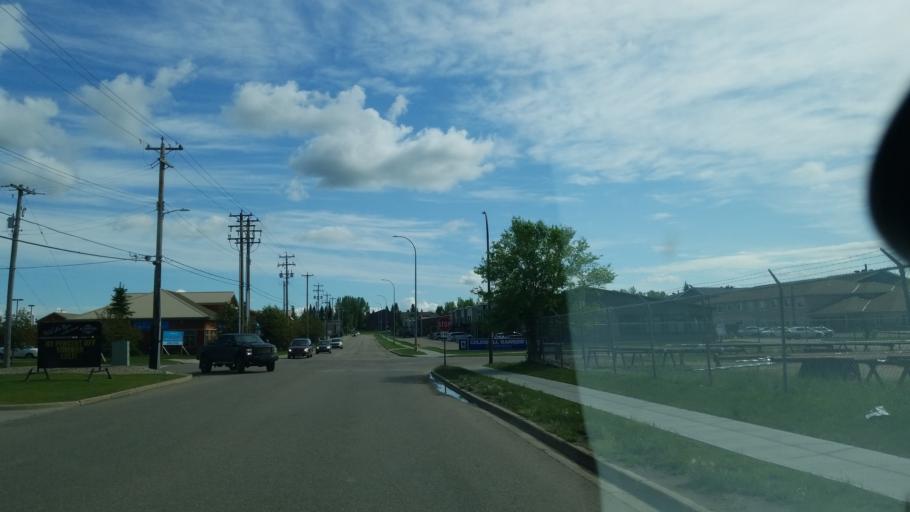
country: CA
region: Saskatchewan
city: Lloydminster
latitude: 53.2739
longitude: -110.0086
